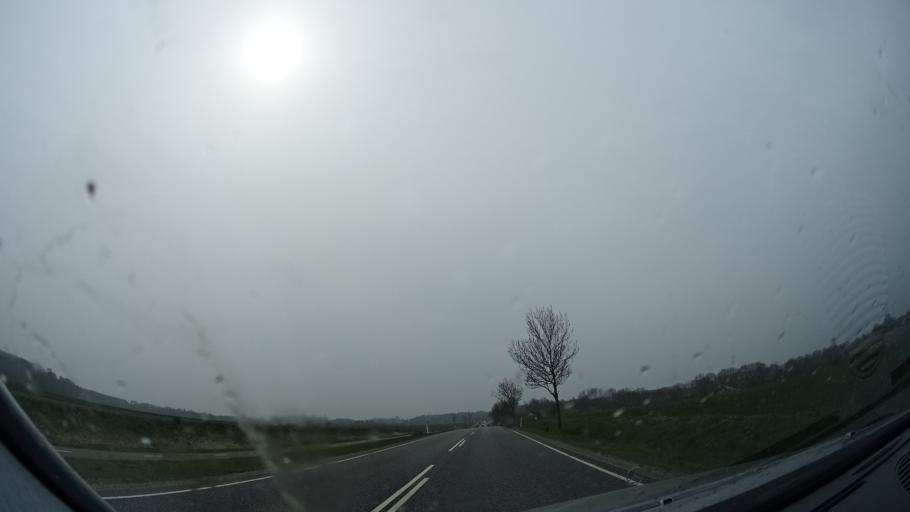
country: DK
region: Zealand
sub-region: Lejre Kommune
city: Ejby
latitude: 55.6761
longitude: 11.8351
